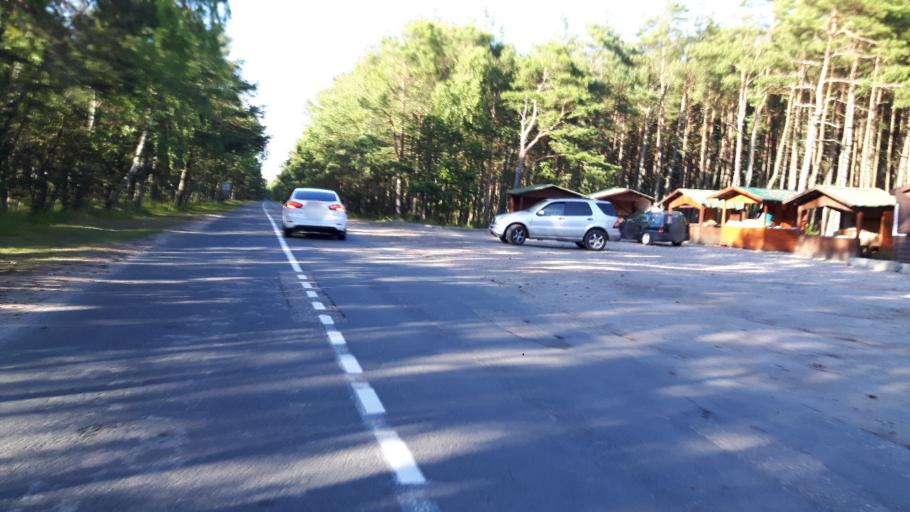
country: LT
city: Nida
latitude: 55.2225
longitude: 20.8920
